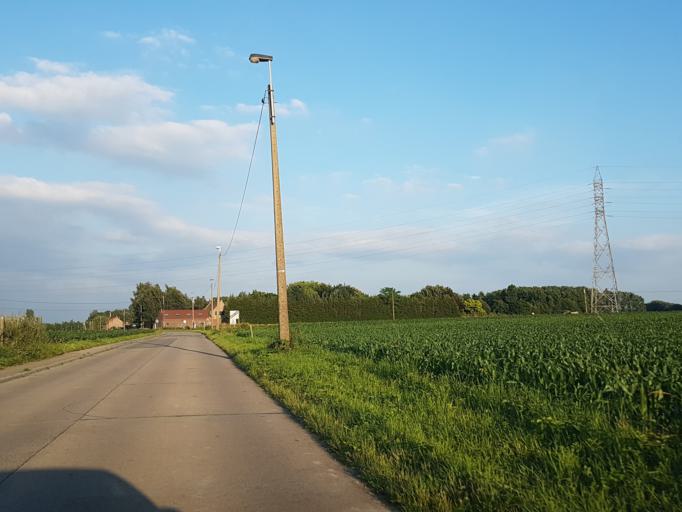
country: BE
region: Flanders
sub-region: Provincie Vlaams-Brabant
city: Ternat
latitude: 50.8654
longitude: 4.1868
